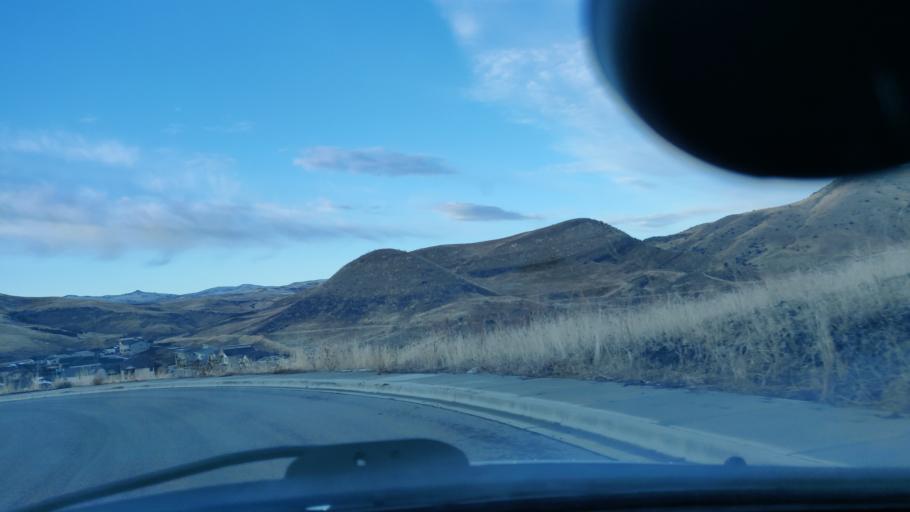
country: US
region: Idaho
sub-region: Ada County
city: Eagle
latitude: 43.7765
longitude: -116.2584
